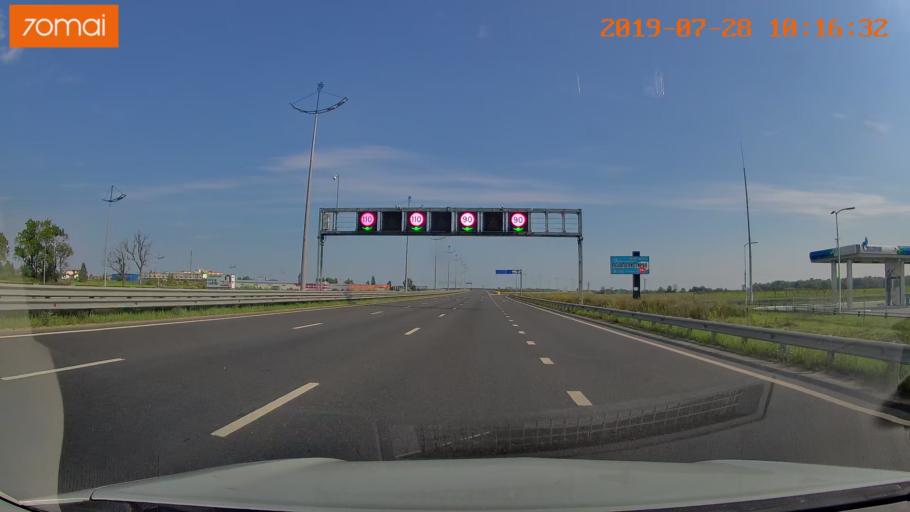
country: RU
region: Kaliningrad
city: Bol'shoe Isakovo
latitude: 54.7275
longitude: 20.5973
